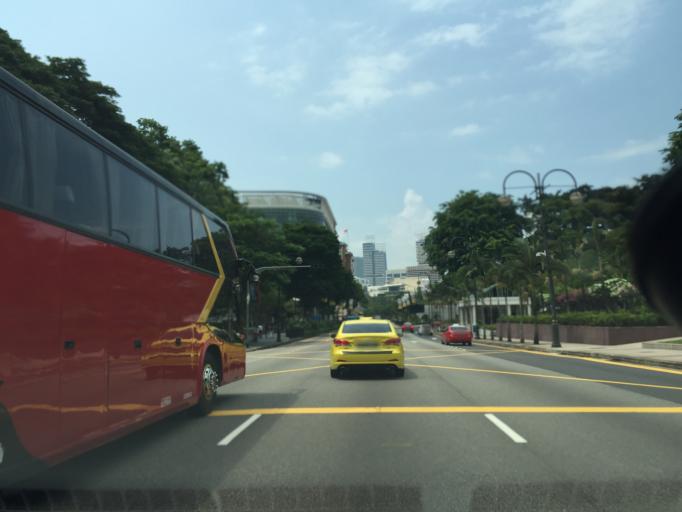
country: SG
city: Singapore
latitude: 1.2998
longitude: 103.8436
